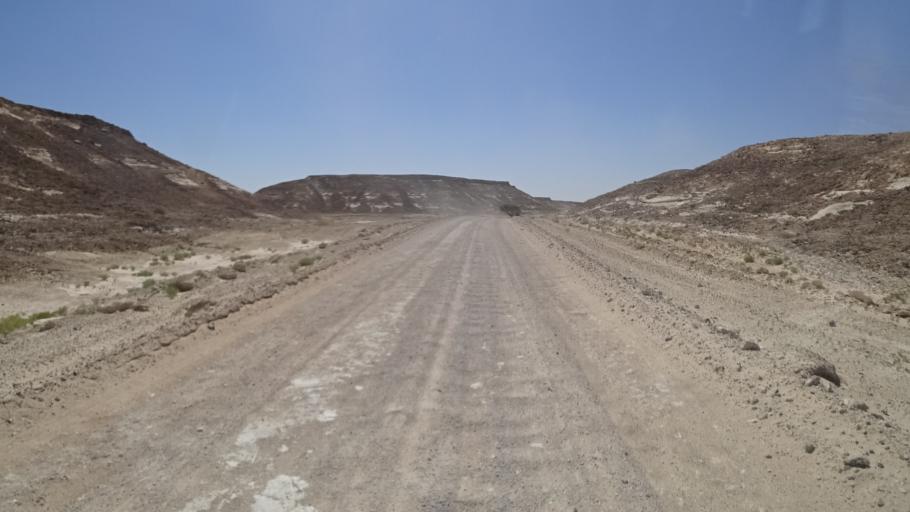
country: OM
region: Zufar
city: Salalah
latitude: 17.4674
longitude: 53.3426
